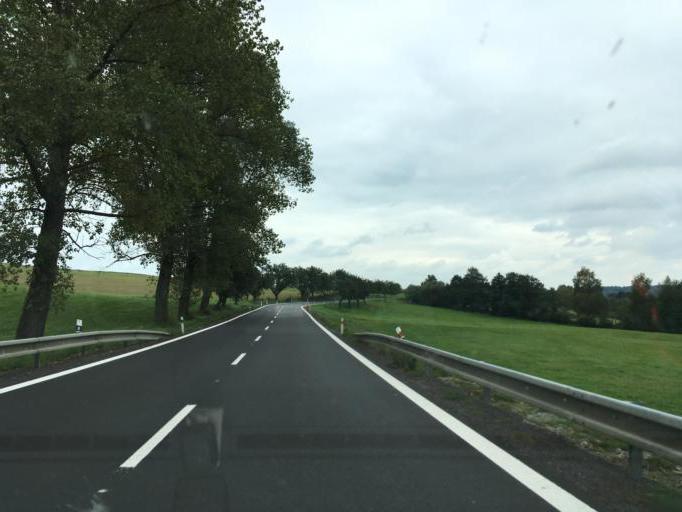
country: CZ
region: Central Bohemia
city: Cechtice
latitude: 49.5868
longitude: 15.0813
